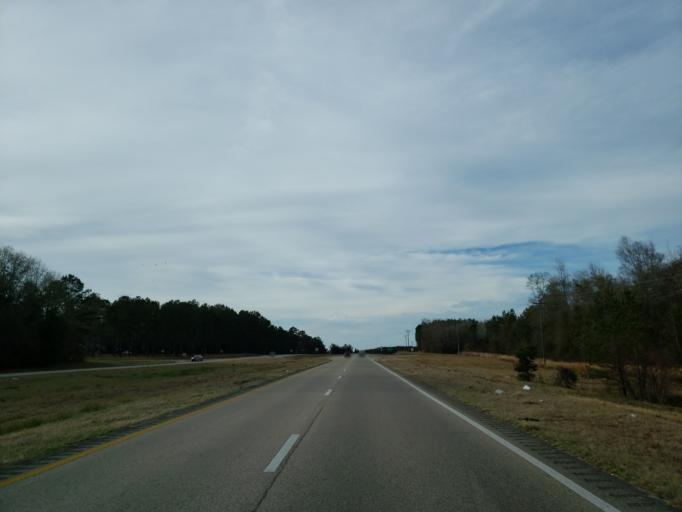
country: US
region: Mississippi
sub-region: Wayne County
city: Waynesboro
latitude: 31.6253
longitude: -88.5864
